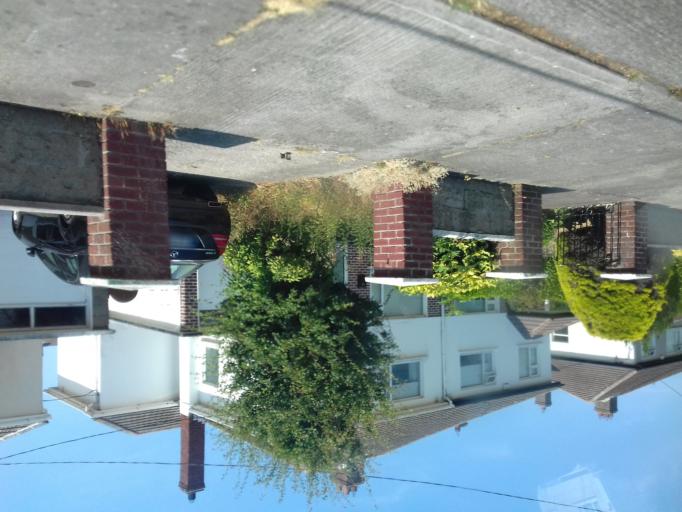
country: IE
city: Bayside
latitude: 53.3894
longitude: -6.1309
